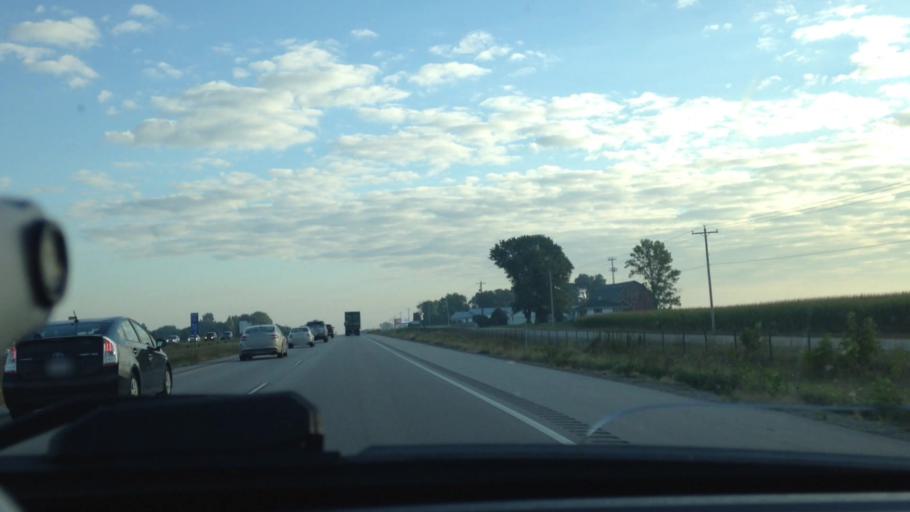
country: US
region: Wisconsin
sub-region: Brown County
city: Wrightstown
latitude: 44.3624
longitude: -88.1811
